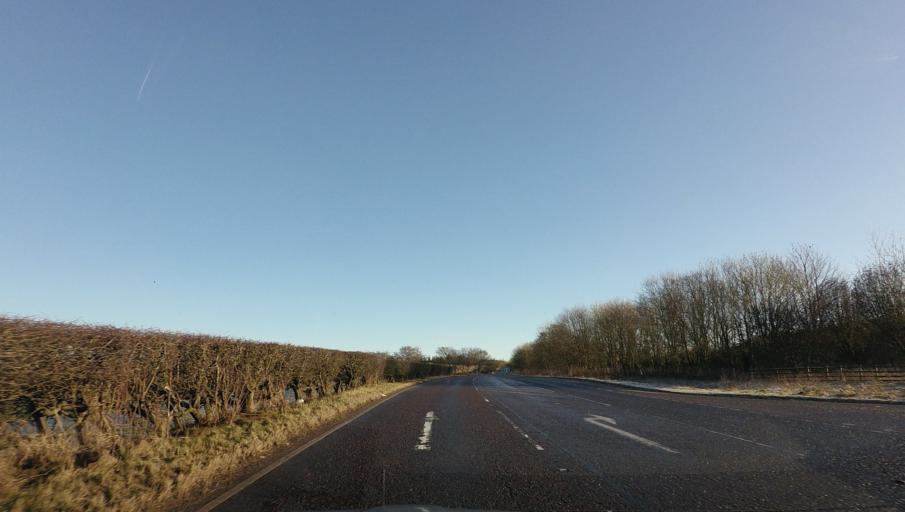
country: GB
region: Scotland
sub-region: North Lanarkshire
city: Shotts
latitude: 55.8084
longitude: -3.7939
